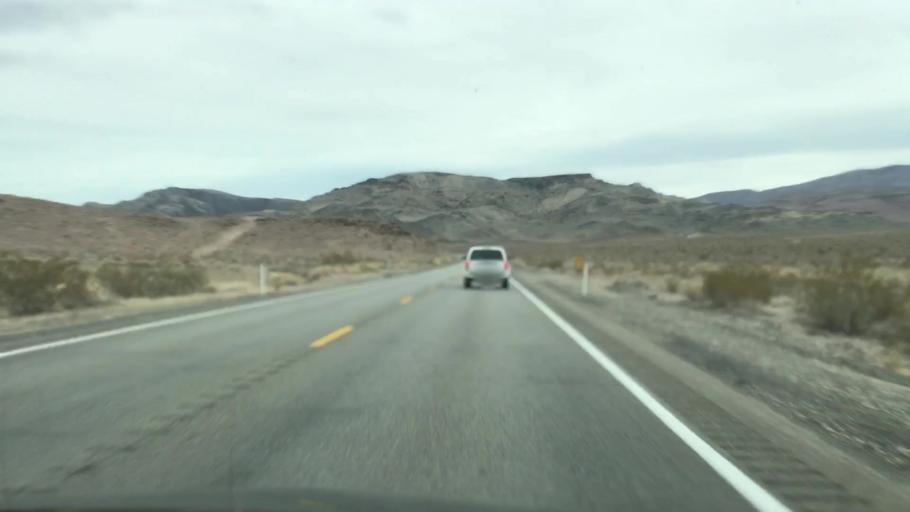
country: US
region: Nevada
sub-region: Nye County
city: Pahrump
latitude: 36.5619
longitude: -116.1026
